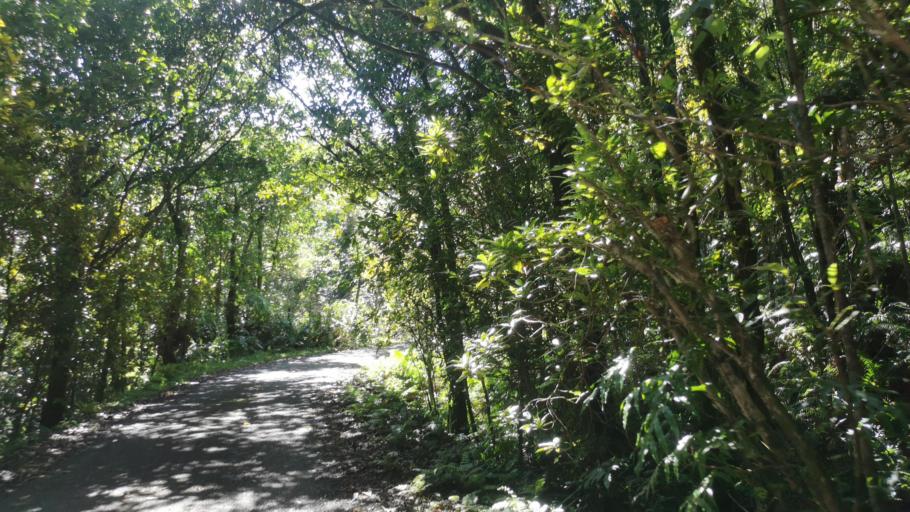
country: RE
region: Reunion
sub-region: Reunion
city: Saint-Philippe
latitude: -21.3562
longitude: 55.7393
